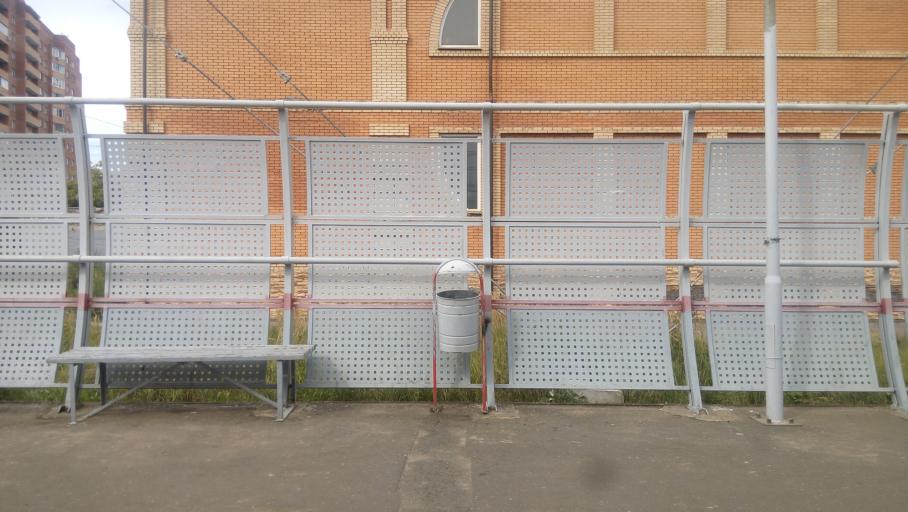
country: RU
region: Moskovskaya
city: Pavlovskiy Posad
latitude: 55.7769
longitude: 38.6732
